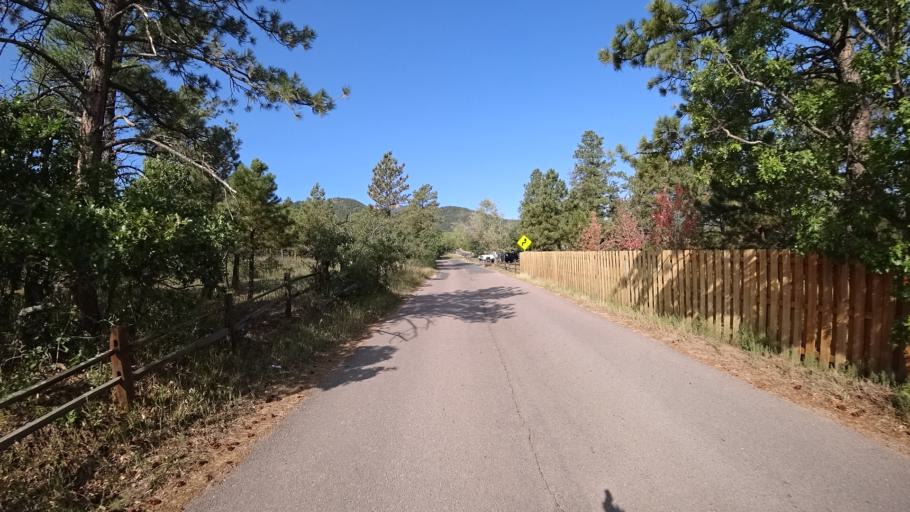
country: US
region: Colorado
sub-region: El Paso County
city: Colorado Springs
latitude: 38.8110
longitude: -104.8676
